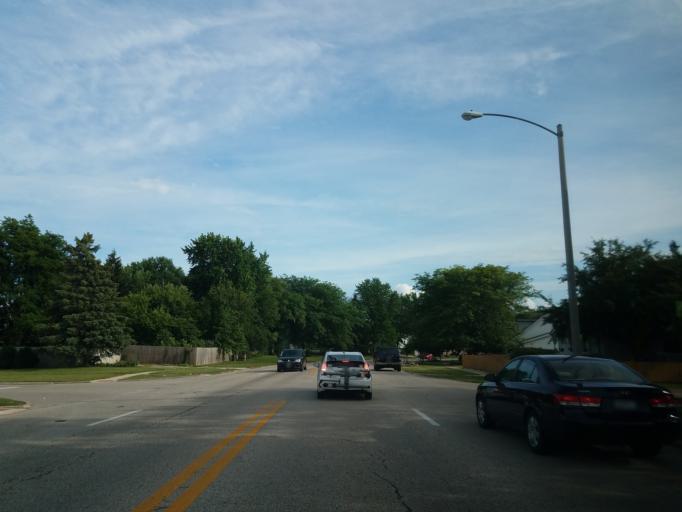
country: US
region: Illinois
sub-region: McLean County
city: Normal
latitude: 40.4997
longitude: -88.9387
